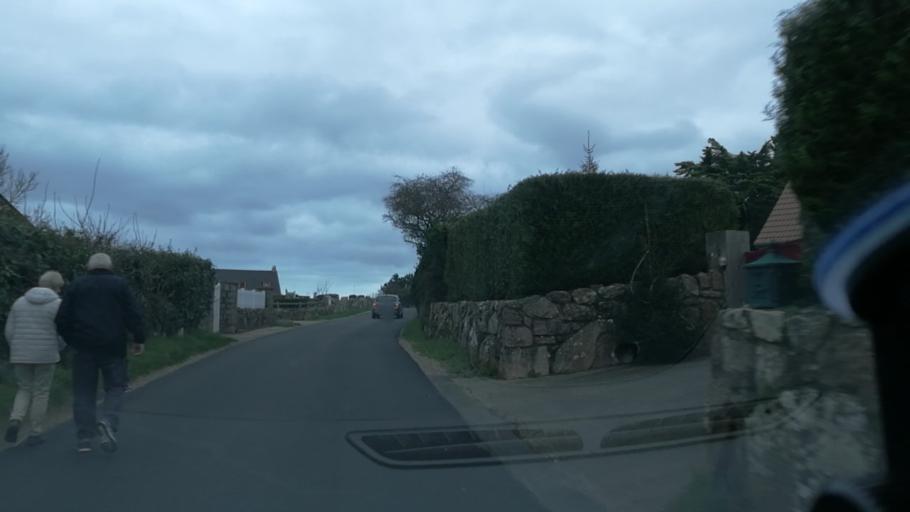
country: FR
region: Lower Normandy
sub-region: Departement de la Manche
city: Fermanville
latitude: 49.6817
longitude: -1.4583
